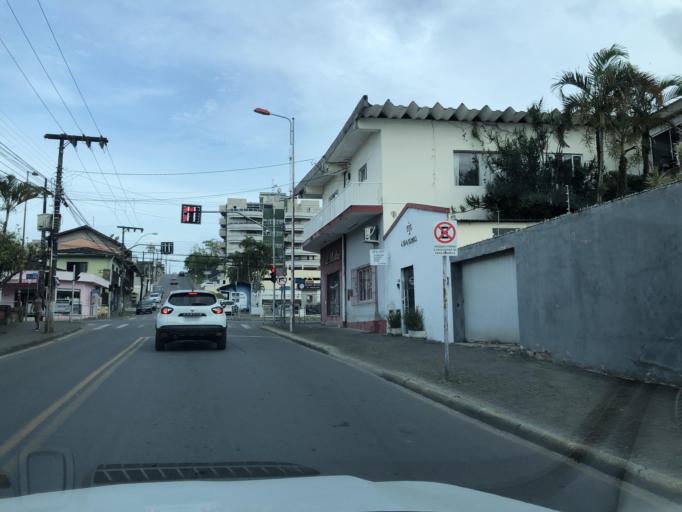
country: BR
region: Santa Catarina
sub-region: Sao Francisco Do Sul
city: Sao Francisco do Sul
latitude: -26.2490
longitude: -48.6360
